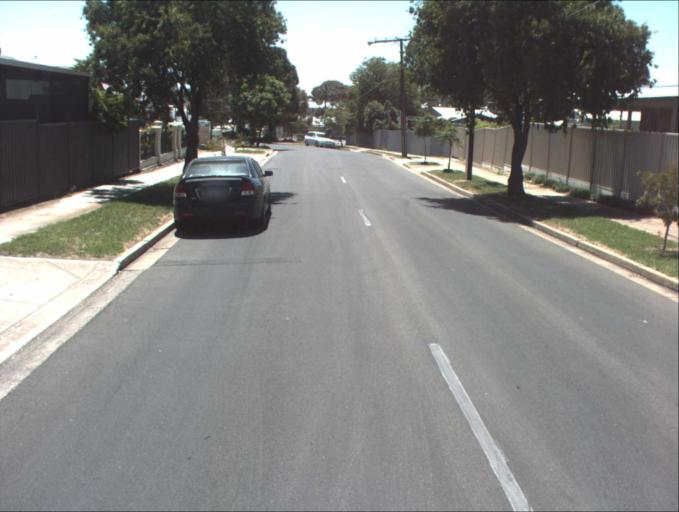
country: AU
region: South Australia
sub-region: Port Adelaide Enfield
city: Enfield
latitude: -34.8664
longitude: 138.6121
